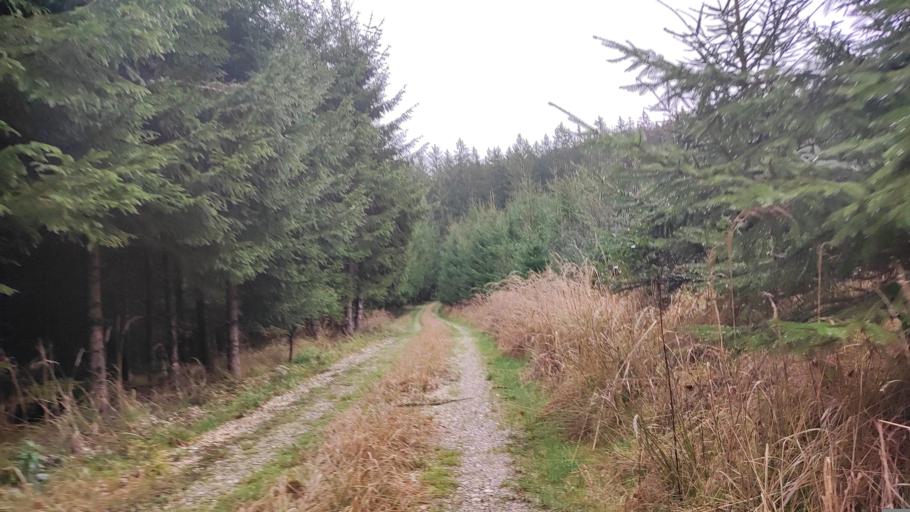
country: DE
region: Bavaria
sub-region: Swabia
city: Dinkelscherben
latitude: 48.3576
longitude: 10.5244
